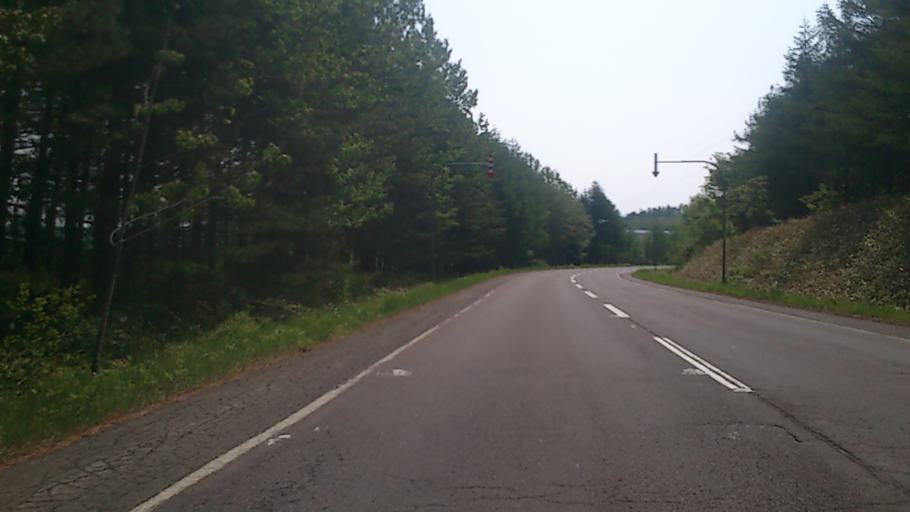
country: JP
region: Hokkaido
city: Kushiro
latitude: 43.4840
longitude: 144.5330
